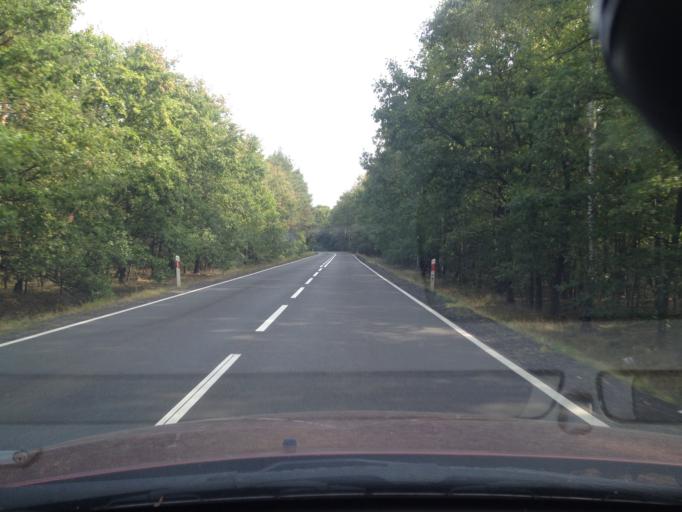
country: PL
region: Lubusz
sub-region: Powiat zaganski
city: Szprotawa
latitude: 51.4572
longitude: 15.6133
